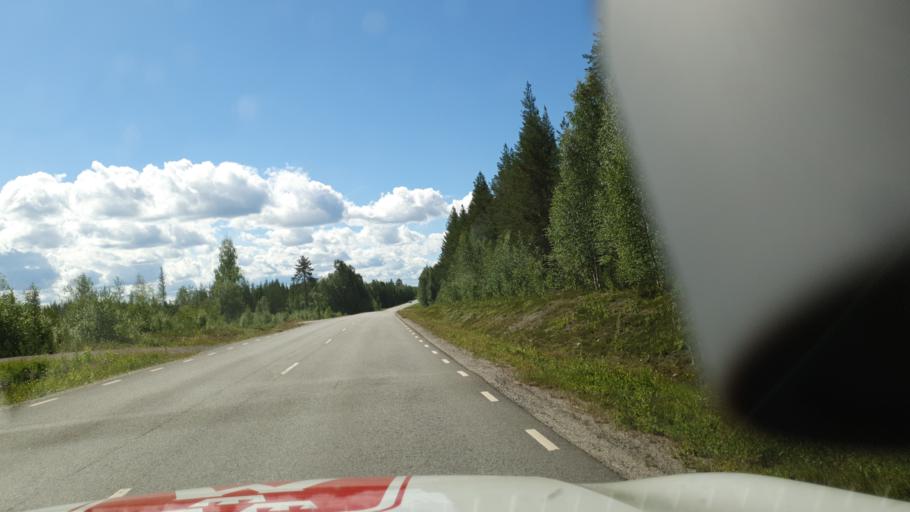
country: SE
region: Vaesterbotten
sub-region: Lycksele Kommun
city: Lycksele
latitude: 64.6847
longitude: 18.6986
